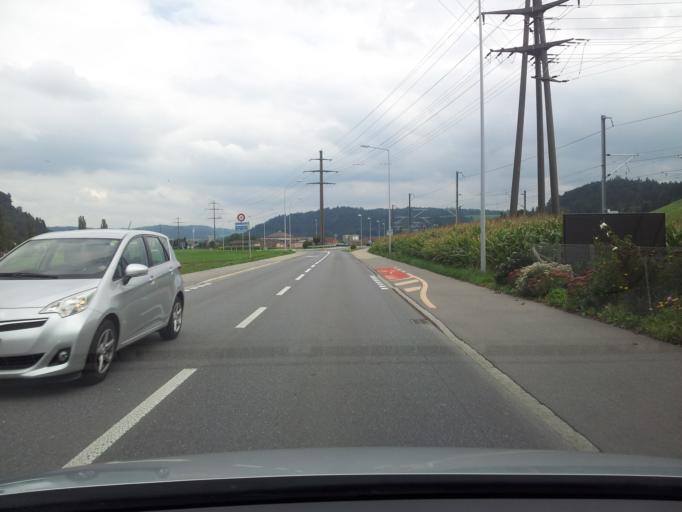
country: CH
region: Lucerne
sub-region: Willisau District
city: Willisau
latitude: 47.1418
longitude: 7.9771
